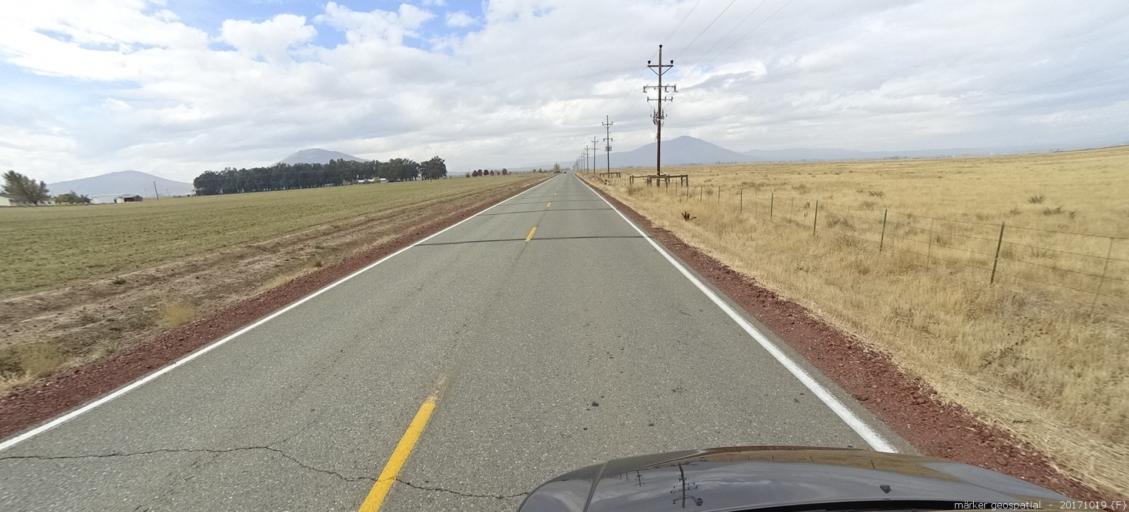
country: US
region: California
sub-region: Shasta County
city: Burney
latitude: 41.0510
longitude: -121.4094
